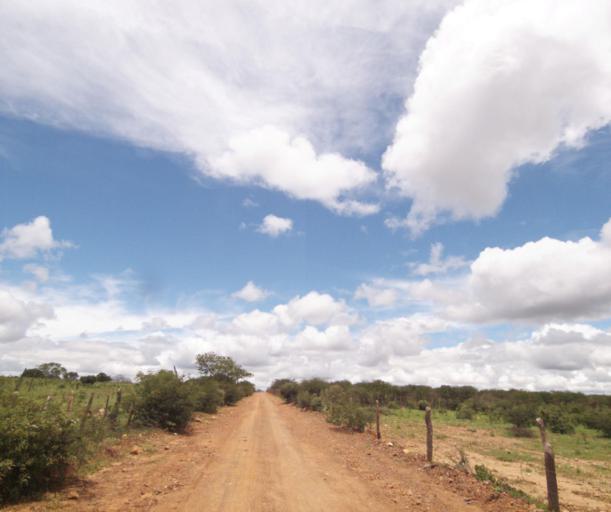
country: BR
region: Bahia
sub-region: Tanhacu
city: Tanhacu
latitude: -14.1903
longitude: -41.0706
